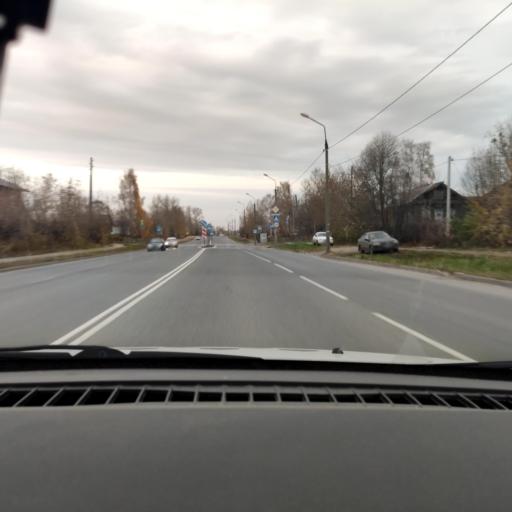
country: RU
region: Perm
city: Polazna
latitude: 58.1196
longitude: 56.4030
